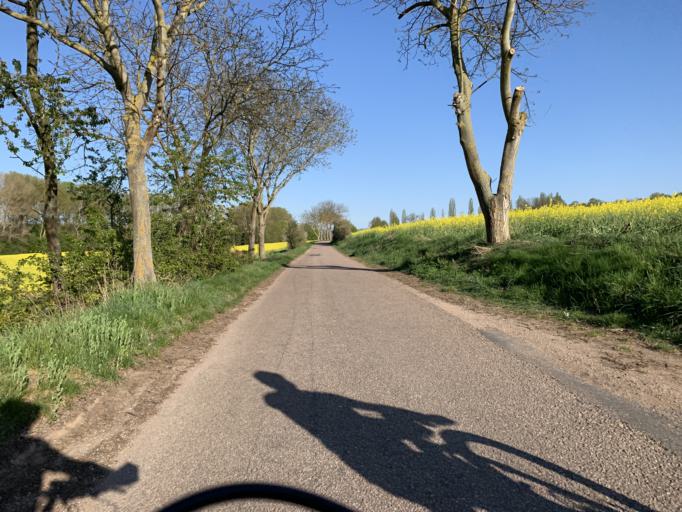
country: DE
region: Rheinland-Pfalz
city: Langenlonsheim
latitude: 49.8881
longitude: 7.8824
